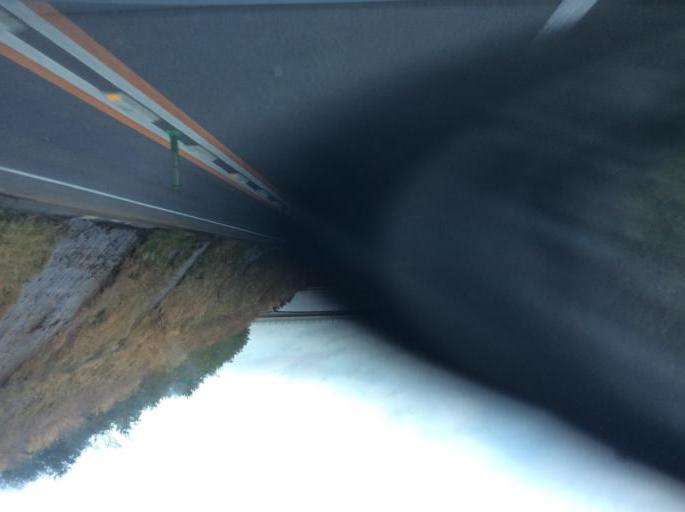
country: JP
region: Fukushima
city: Namie
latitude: 37.2666
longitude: 140.9871
